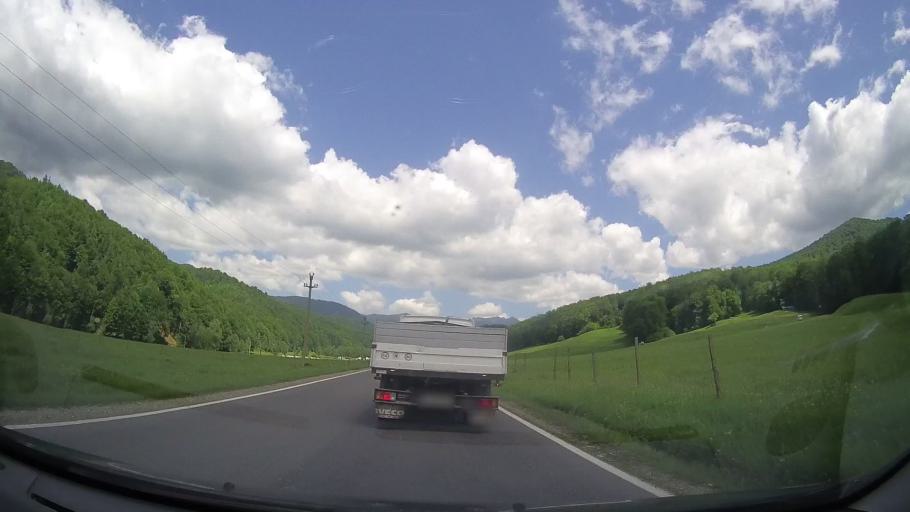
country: RO
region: Prahova
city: Maneciu
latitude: 45.4202
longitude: 25.9430
